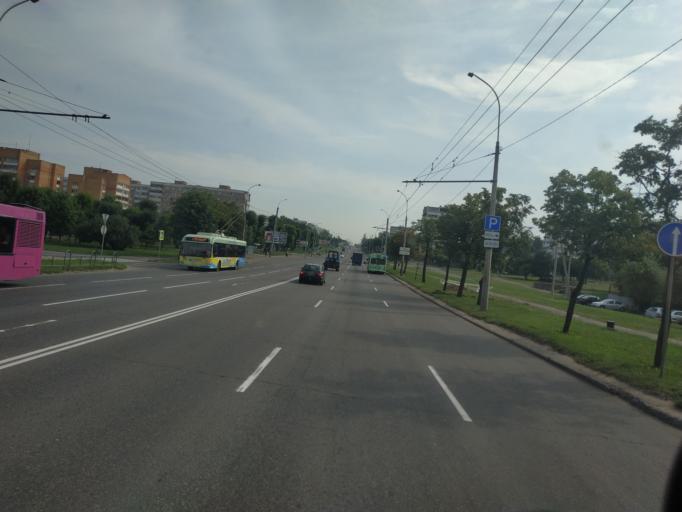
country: BY
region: Mogilev
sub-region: Mahilyowski Rayon
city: Veyno
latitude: 53.8699
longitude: 30.3680
